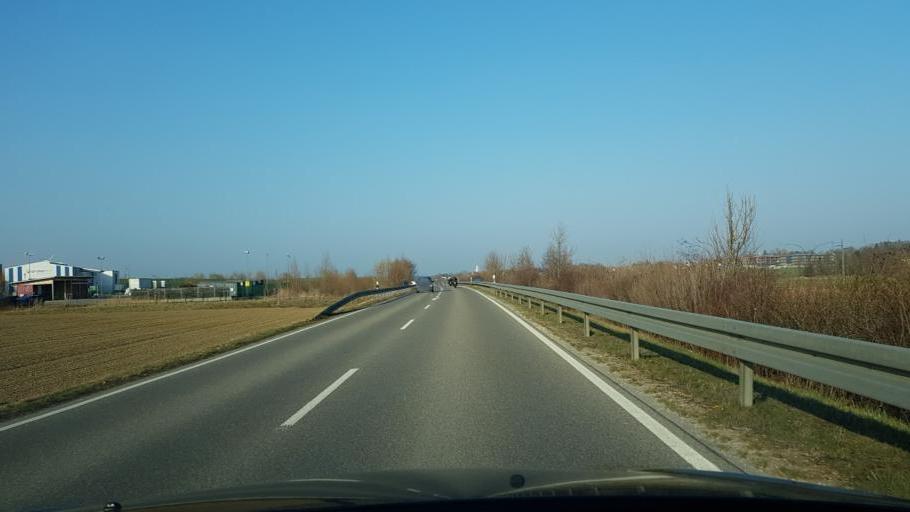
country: DE
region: Bavaria
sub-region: Upper Bavaria
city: Odelzhausen
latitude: 48.3006
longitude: 11.1795
